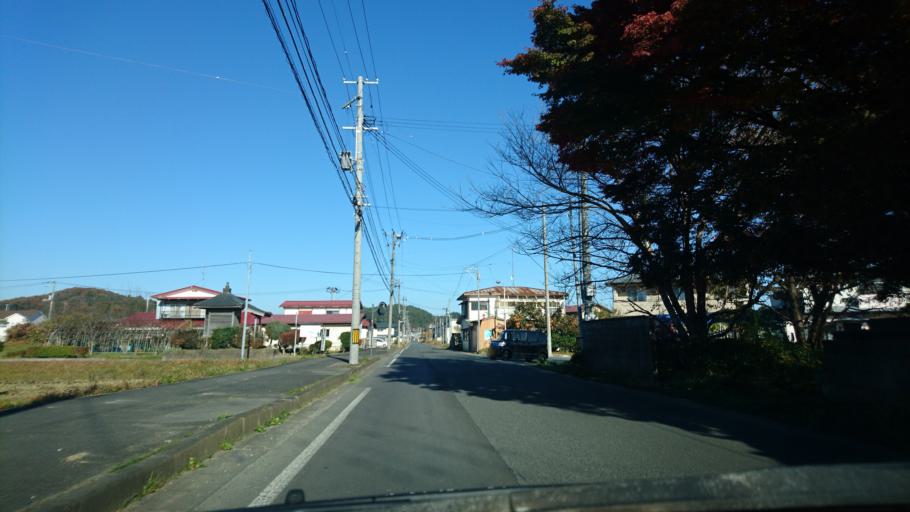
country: JP
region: Iwate
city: Mizusawa
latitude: 39.0353
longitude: 141.1244
